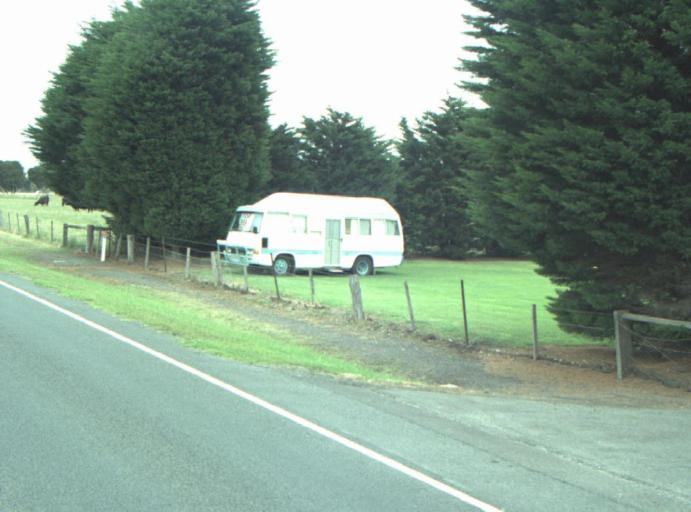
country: AU
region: Victoria
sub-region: Greater Geelong
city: Leopold
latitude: -38.1712
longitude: 144.4216
